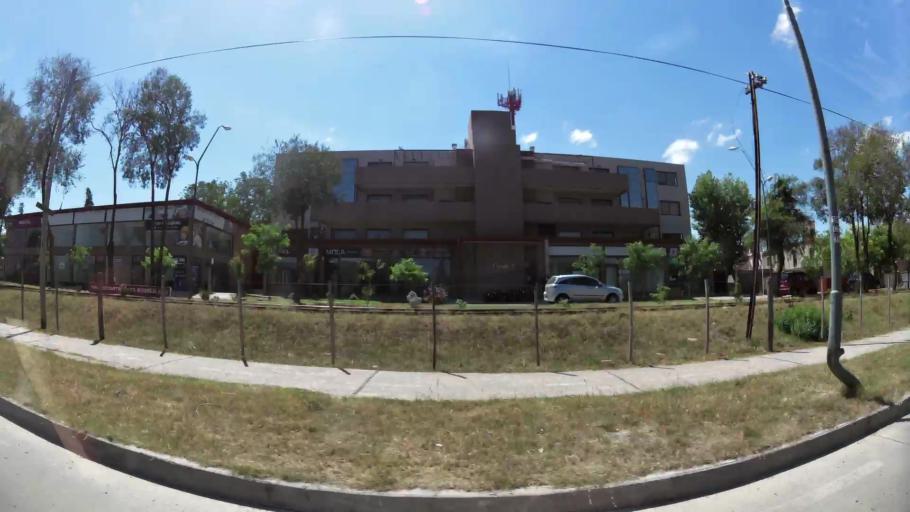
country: AR
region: Cordoba
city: Villa Allende
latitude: -31.3352
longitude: -64.2645
